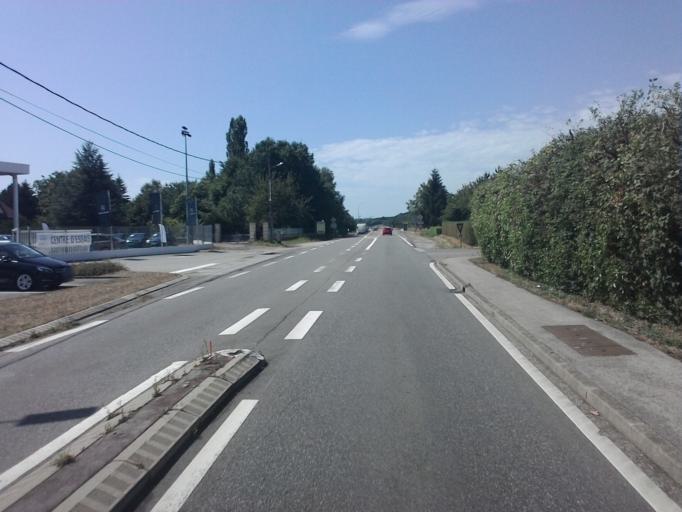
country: FR
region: Franche-Comte
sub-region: Departement du Jura
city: Montmorot
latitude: 46.6604
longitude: 5.5178
